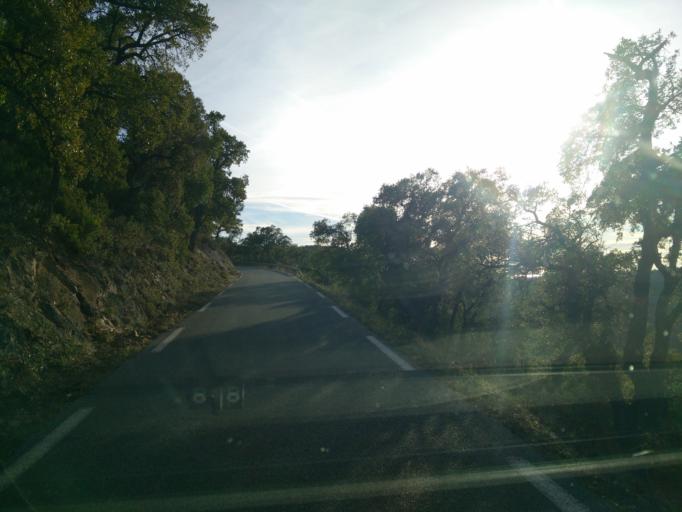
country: FR
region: Provence-Alpes-Cote d'Azur
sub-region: Departement du Var
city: Collobrieres
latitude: 43.1944
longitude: 6.3149
